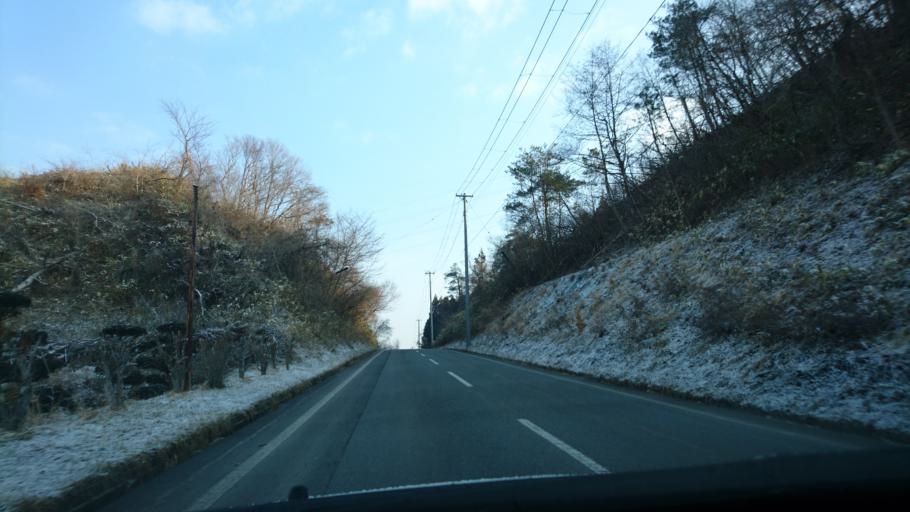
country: JP
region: Iwate
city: Ichinoseki
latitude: 38.9196
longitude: 141.3836
